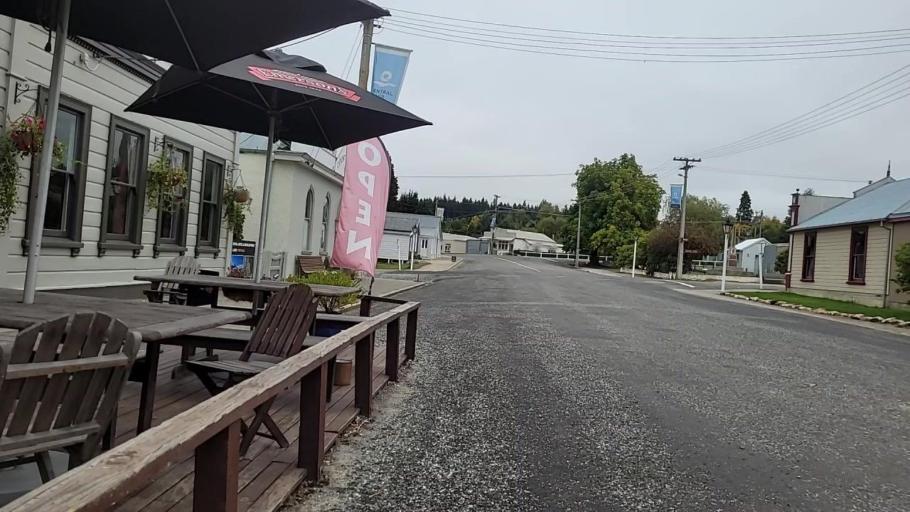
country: NZ
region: Otago
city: Oamaru
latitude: -45.0235
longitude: 170.1478
